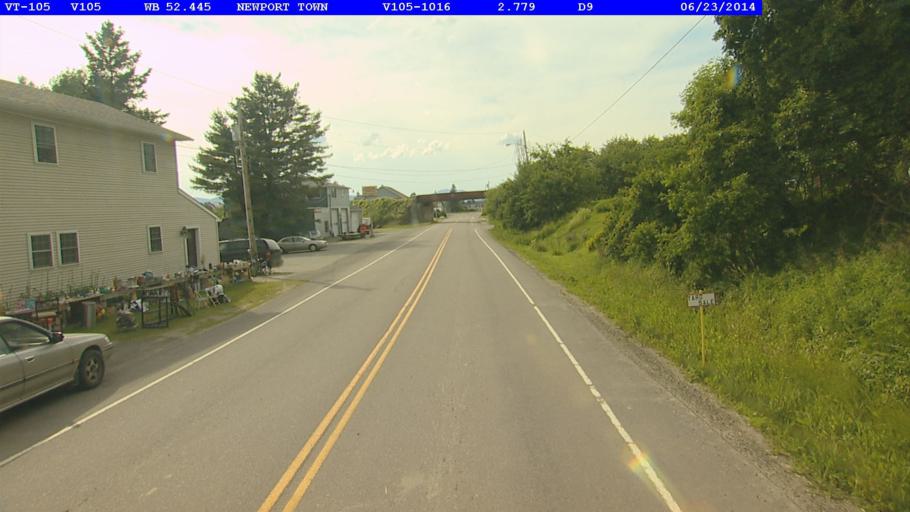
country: US
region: Vermont
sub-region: Orleans County
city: Newport
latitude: 44.9487
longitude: -72.3033
